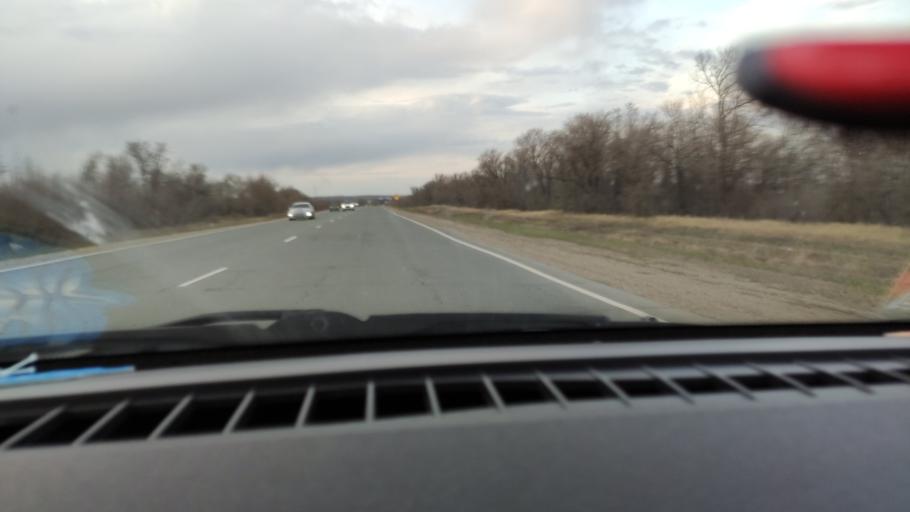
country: RU
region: Saratov
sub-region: Saratovskiy Rayon
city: Saratov
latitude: 51.7164
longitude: 46.0258
